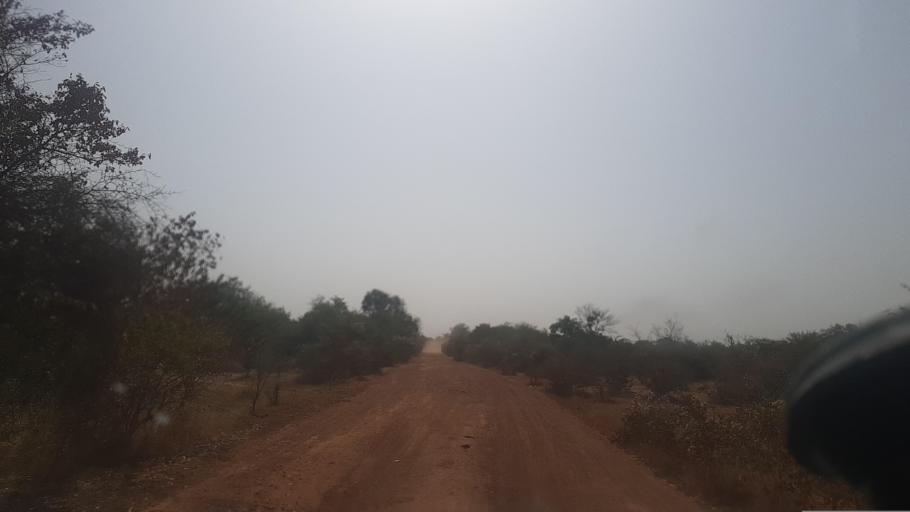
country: ML
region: Segou
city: Baroueli
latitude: 13.0776
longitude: -6.4845
